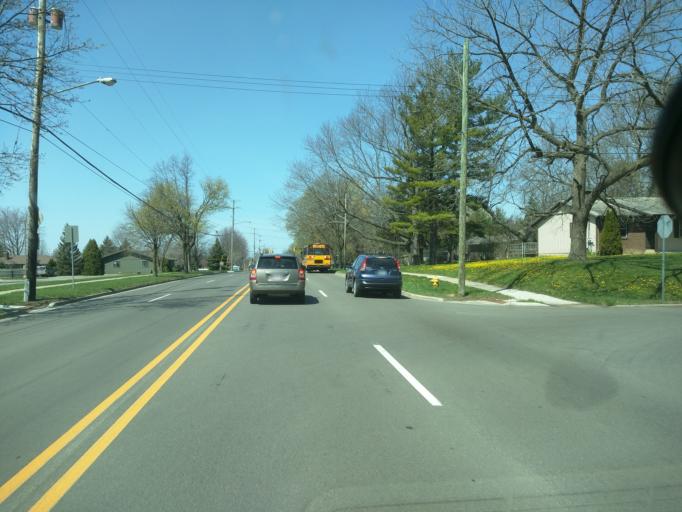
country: US
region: Michigan
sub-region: Kent County
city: East Grand Rapids
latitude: 42.9270
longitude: -85.5967
